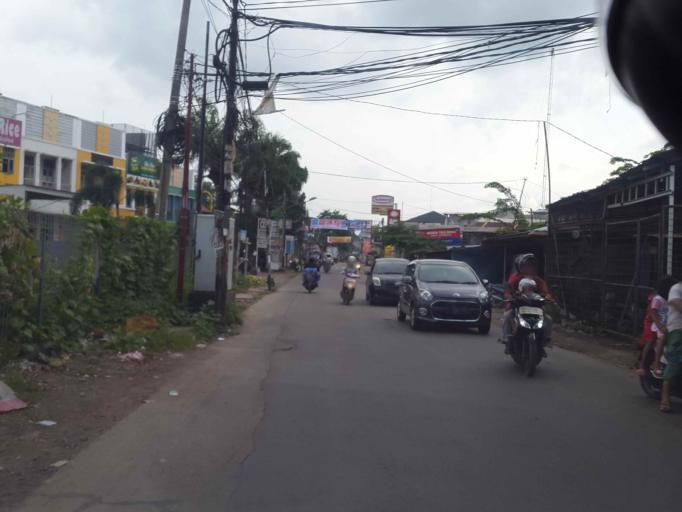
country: ID
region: West Java
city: Bekasi
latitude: -6.3078
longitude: 106.9552
